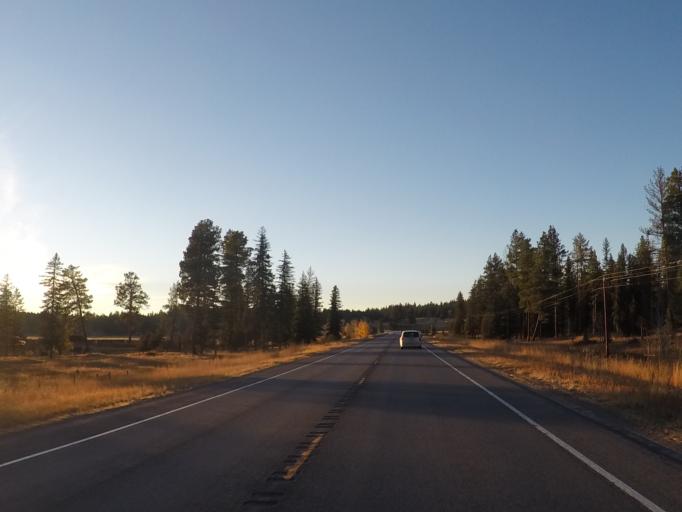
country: US
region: Montana
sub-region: Lewis and Clark County
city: Lincoln
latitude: 47.0034
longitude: -113.0425
